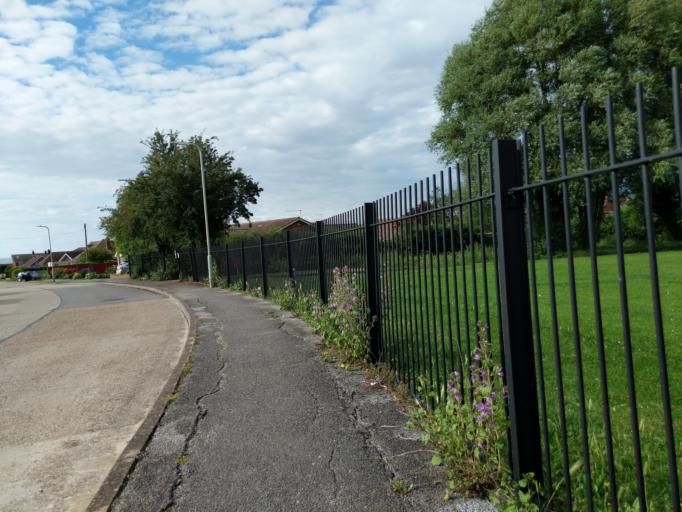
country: GB
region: England
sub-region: Kent
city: Whitstable
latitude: 51.3467
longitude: 1.0111
